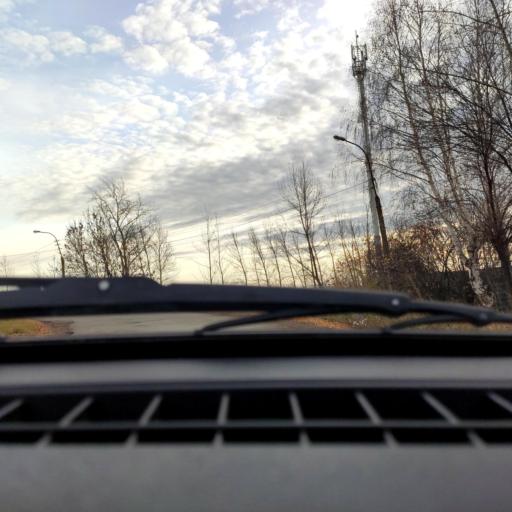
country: RU
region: Bashkortostan
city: Blagoveshchensk
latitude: 54.9000
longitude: 56.1523
